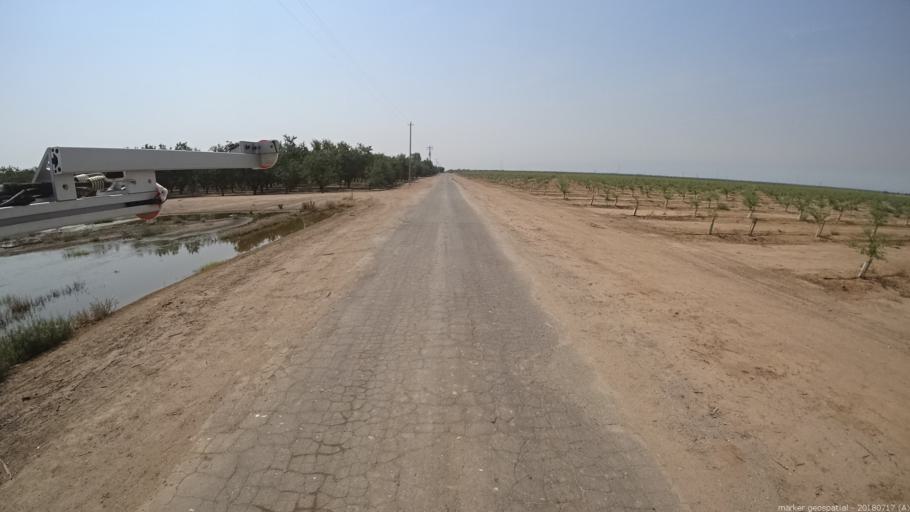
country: US
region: California
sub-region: Madera County
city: Fairmead
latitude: 37.1316
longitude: -120.1202
